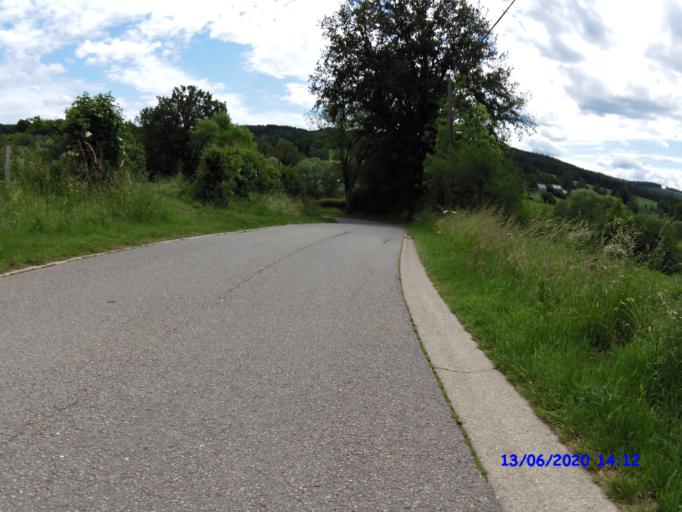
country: BE
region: Wallonia
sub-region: Province de Liege
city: Stavelot
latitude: 50.4130
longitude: 5.9680
